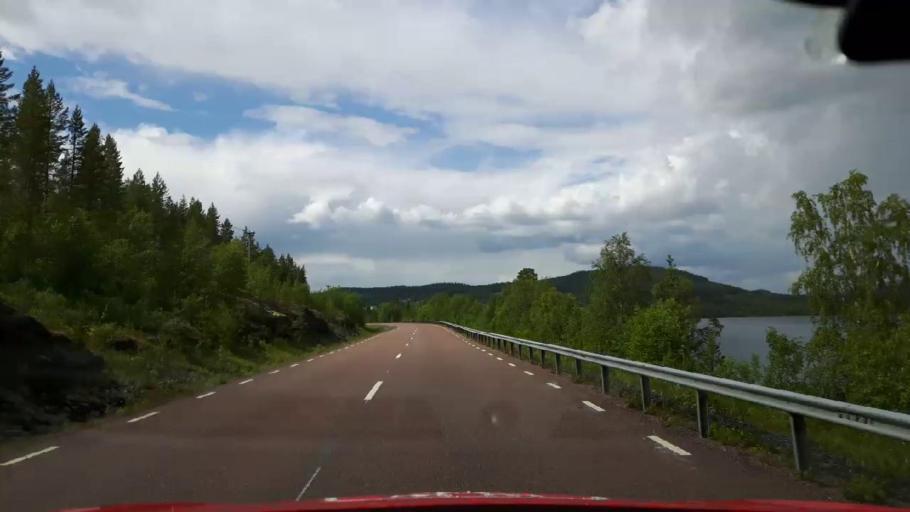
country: SE
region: Jaemtland
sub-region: Krokoms Kommun
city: Valla
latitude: 63.8995
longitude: 14.2425
